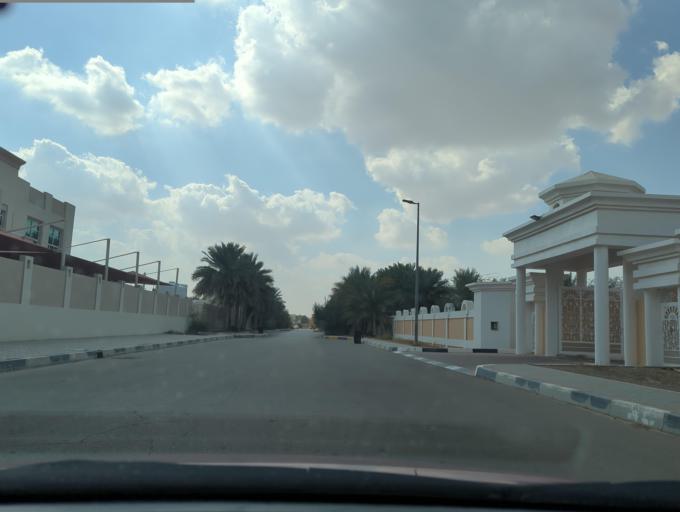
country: AE
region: Abu Dhabi
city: Al Ain
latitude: 24.1549
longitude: 55.6577
